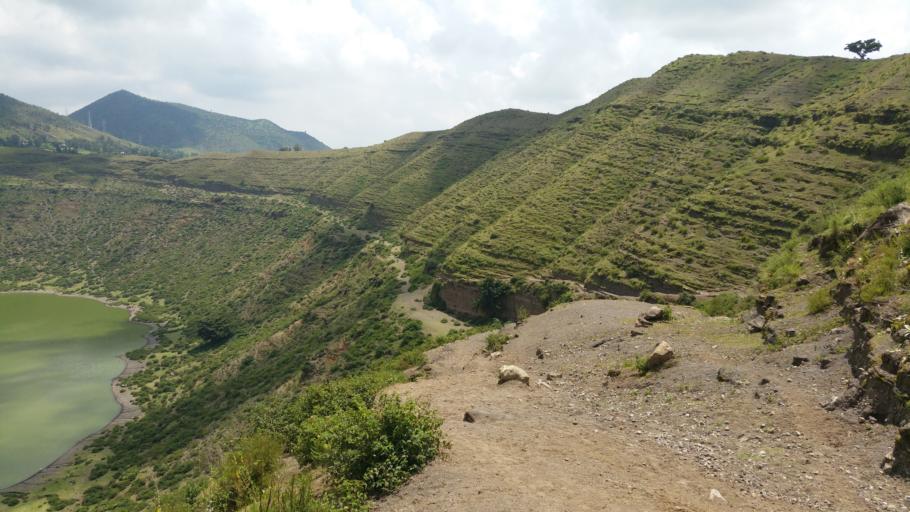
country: ET
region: Oromiya
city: Bishoftu
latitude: 8.6925
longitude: 38.9817
